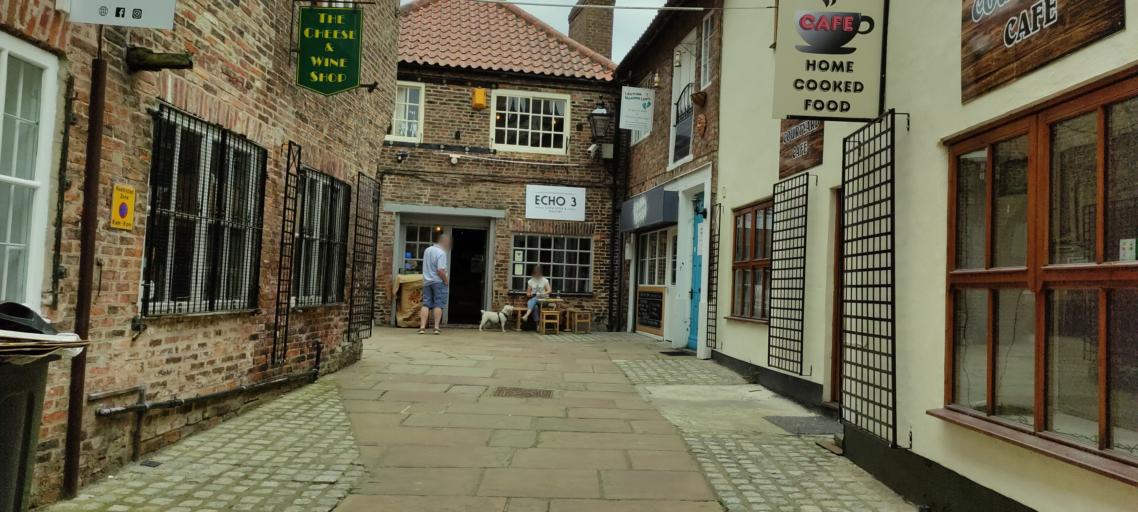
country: GB
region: England
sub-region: Darlington
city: Darlington
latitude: 54.5247
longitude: -1.5561
